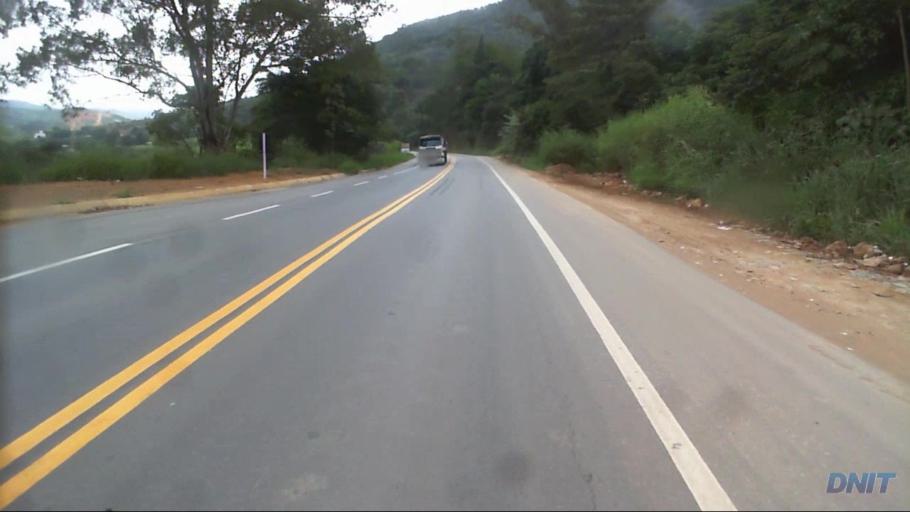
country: BR
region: Minas Gerais
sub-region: Nova Era
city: Nova Era
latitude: -19.7293
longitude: -43.0147
